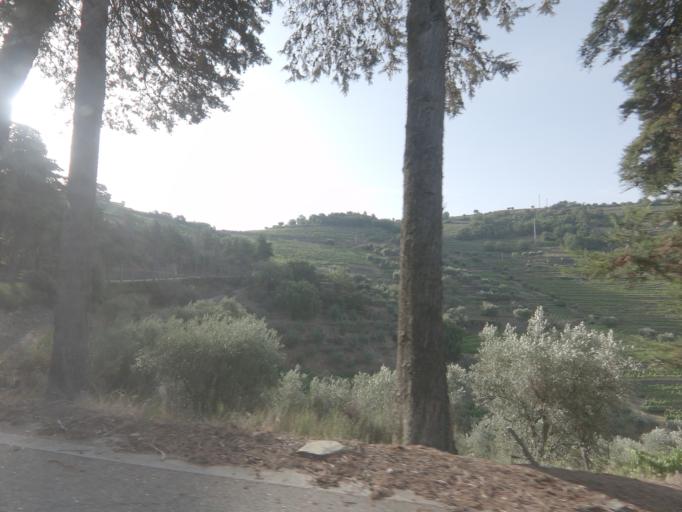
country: PT
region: Vila Real
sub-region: Sabrosa
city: Vilela
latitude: 41.2061
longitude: -7.5311
